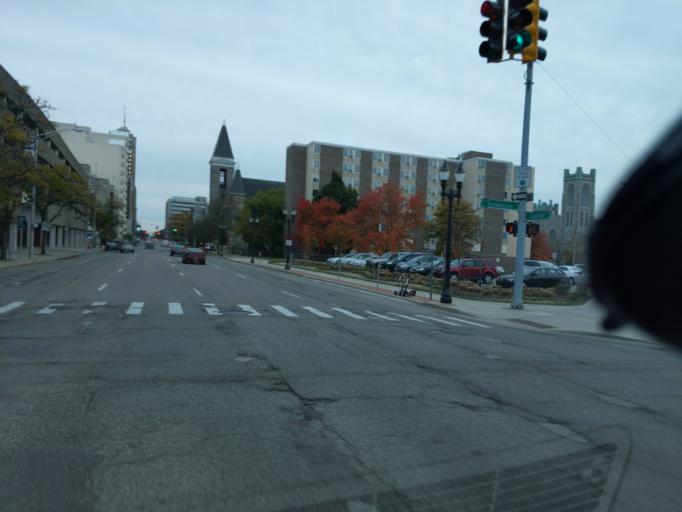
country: US
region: Michigan
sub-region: Ingham County
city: Lansing
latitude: 42.7373
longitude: -84.5538
